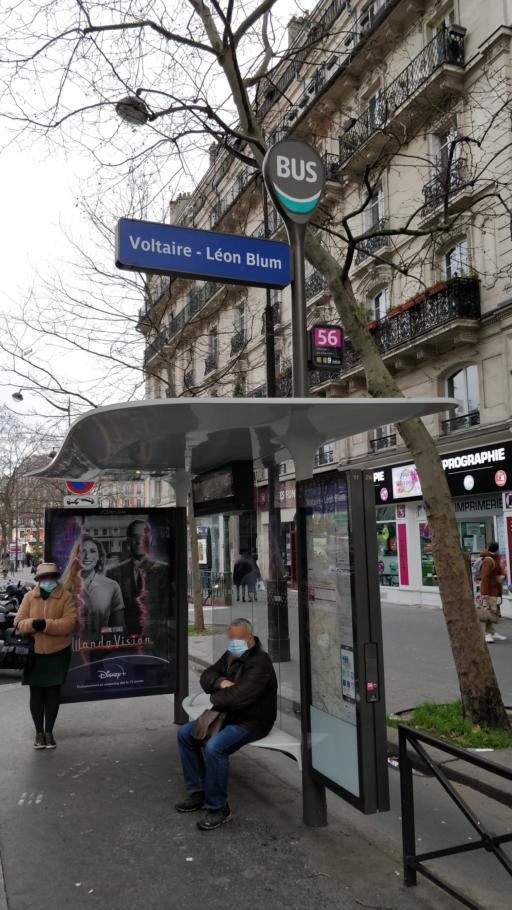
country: FR
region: Ile-de-France
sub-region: Paris
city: Paris
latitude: 48.8586
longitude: 2.3786
